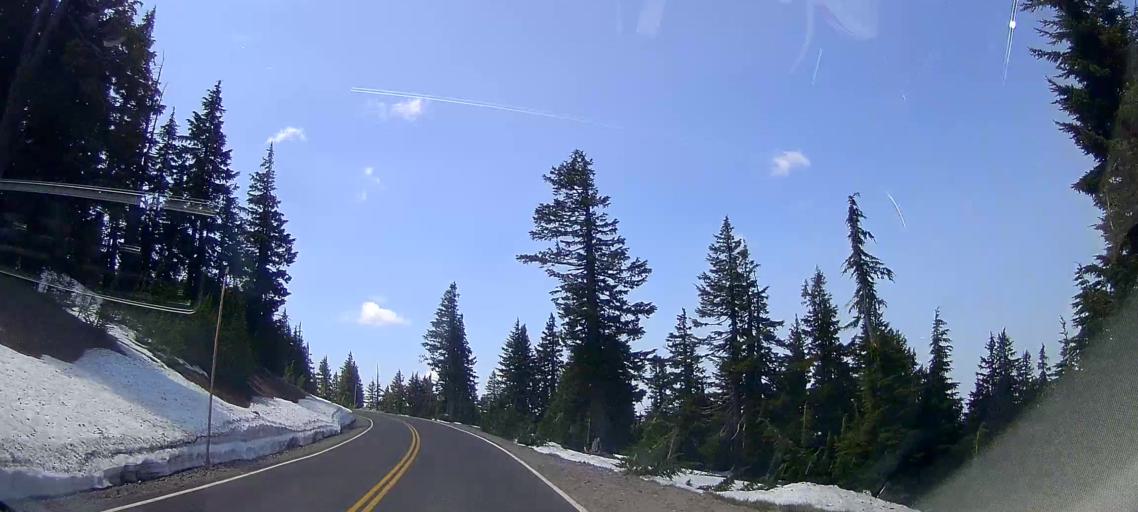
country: US
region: Oregon
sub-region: Jackson County
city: Shady Cove
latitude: 42.9785
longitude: -122.1419
